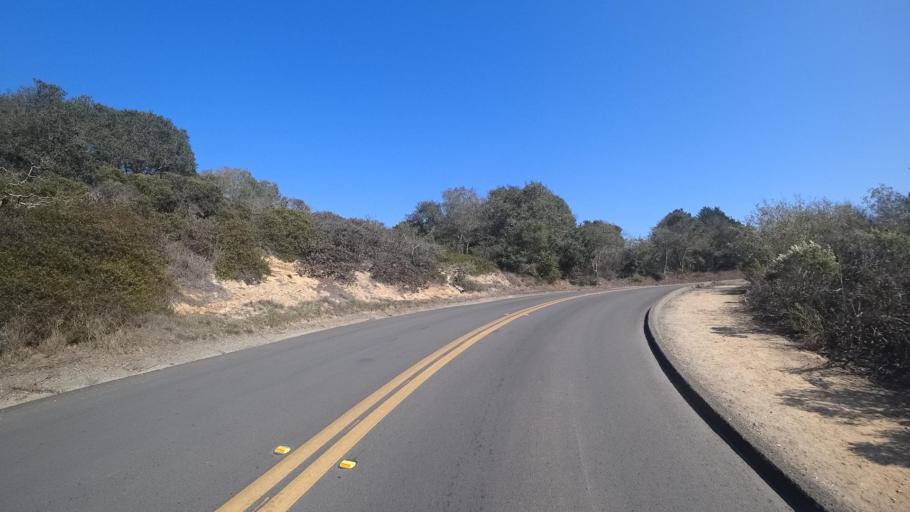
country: US
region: California
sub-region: Monterey County
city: Prunedale
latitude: 36.8022
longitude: -121.6808
